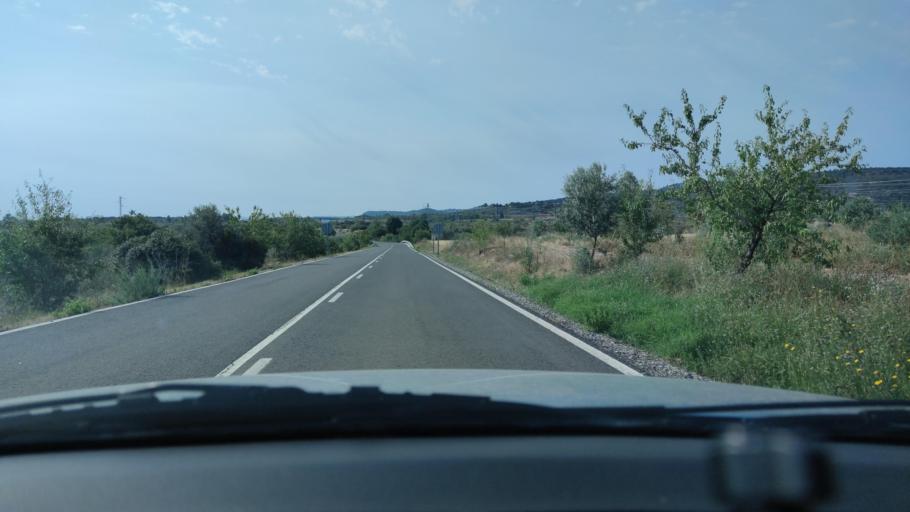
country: ES
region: Catalonia
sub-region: Provincia de Lleida
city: Arbeca
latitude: 41.4864
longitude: 0.8775
